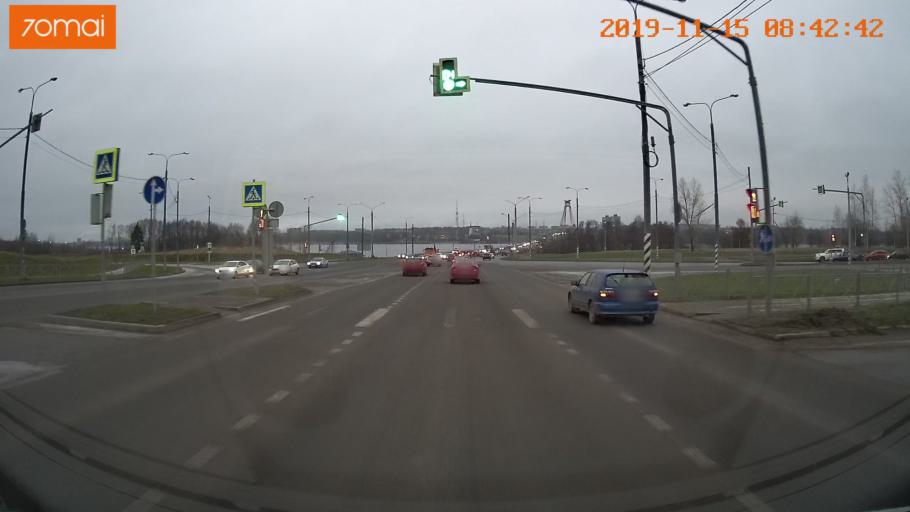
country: RU
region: Vologda
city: Cherepovets
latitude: 59.1047
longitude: 37.9068
